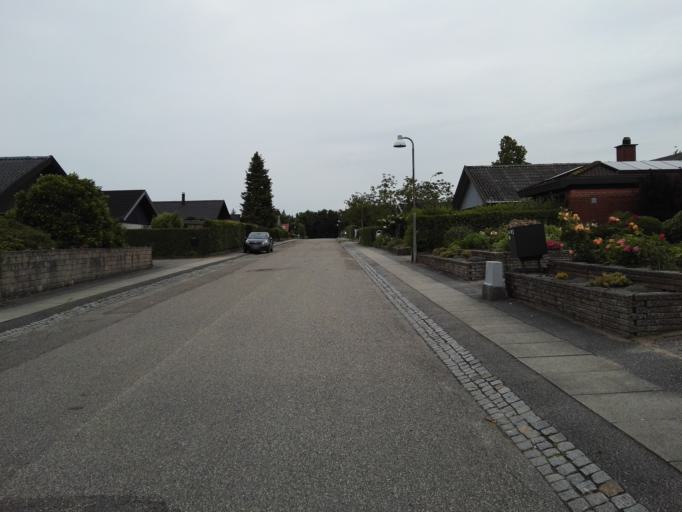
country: DK
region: Zealand
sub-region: Roskilde Kommune
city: Jyllinge
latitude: 55.7460
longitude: 12.1197
